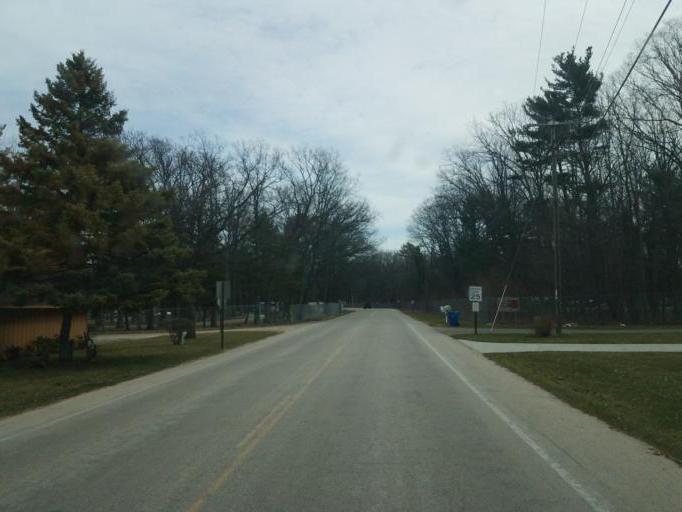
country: US
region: Michigan
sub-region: Oceana County
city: Hart
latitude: 43.6610
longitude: -86.4982
